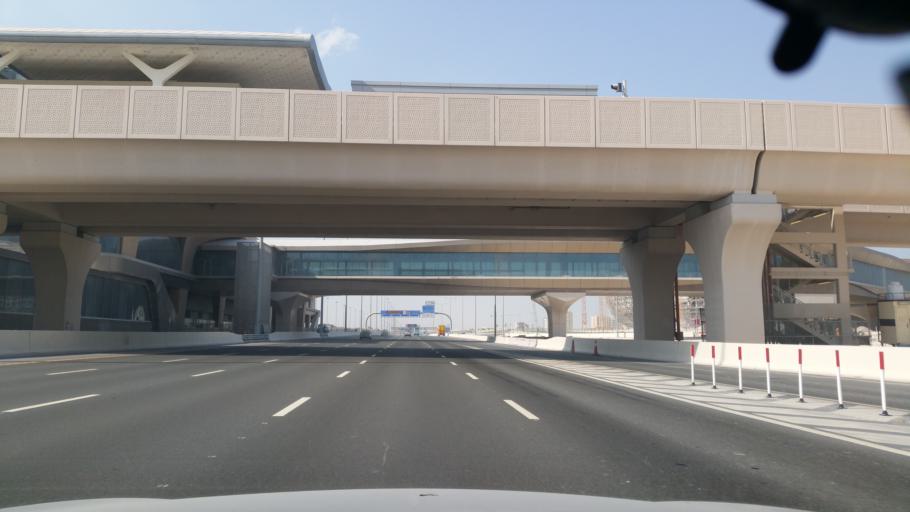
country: QA
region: Baladiyat Umm Salal
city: Umm Salal Muhammad
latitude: 25.4137
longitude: 51.4885
